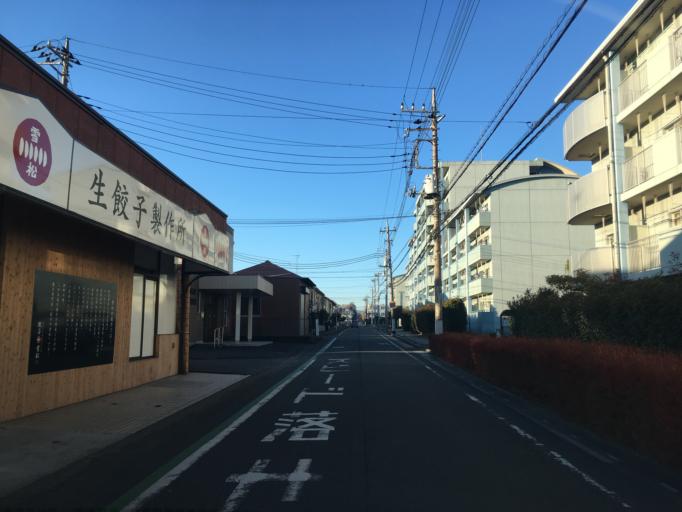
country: JP
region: Saitama
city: Sayama
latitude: 35.8255
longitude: 139.3987
